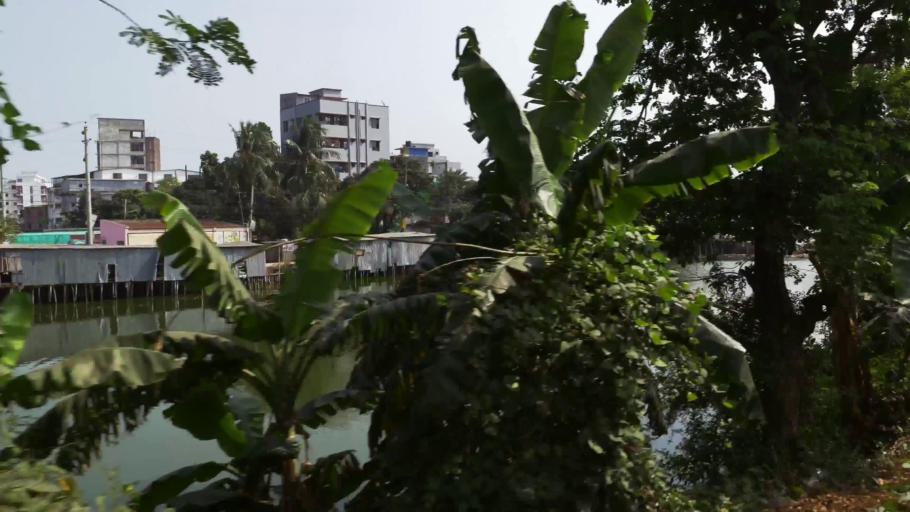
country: BD
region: Dhaka
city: Tungi
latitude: 23.8886
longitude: 90.4072
